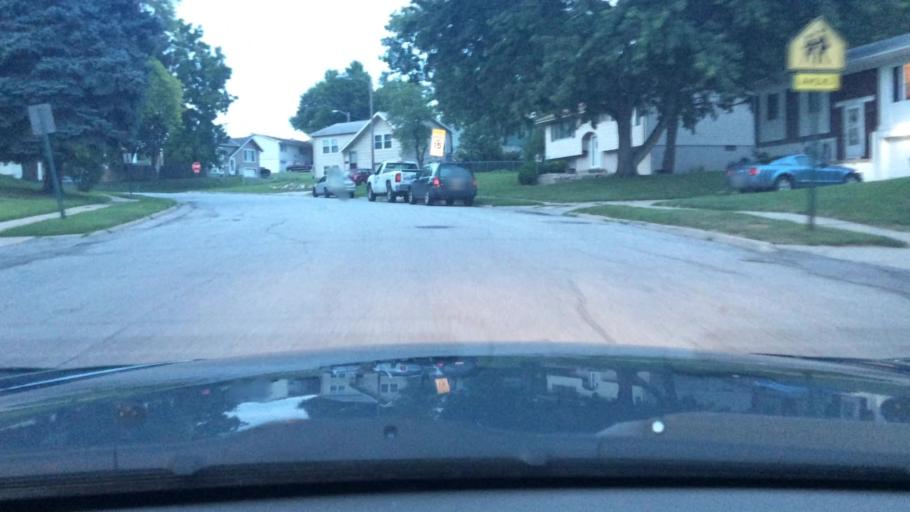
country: US
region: Nebraska
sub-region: Sarpy County
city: La Vista
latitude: 41.1850
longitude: -96.0357
